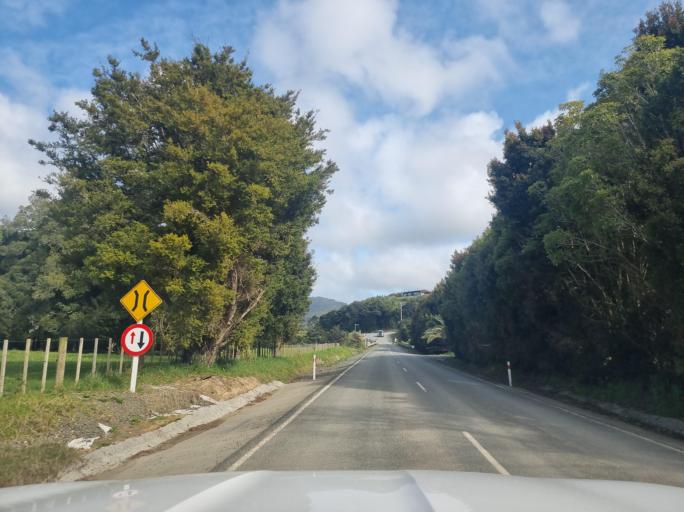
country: NZ
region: Auckland
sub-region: Auckland
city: Wellsford
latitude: -36.0996
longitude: 174.5021
